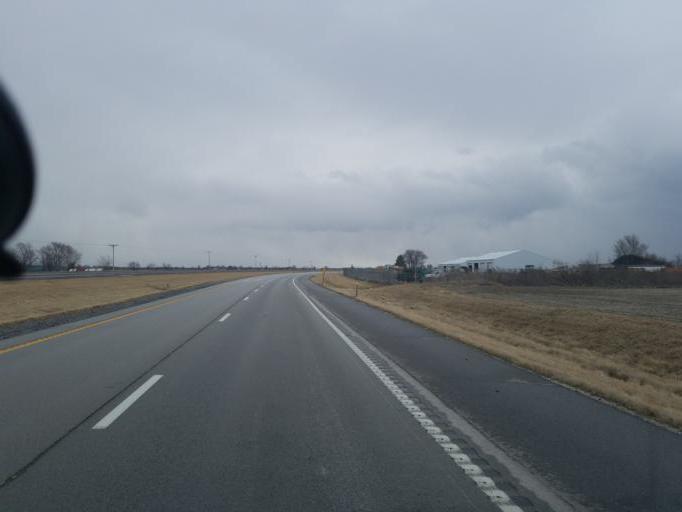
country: US
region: Missouri
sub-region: Macon County
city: Macon
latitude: 39.8197
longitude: -92.4729
